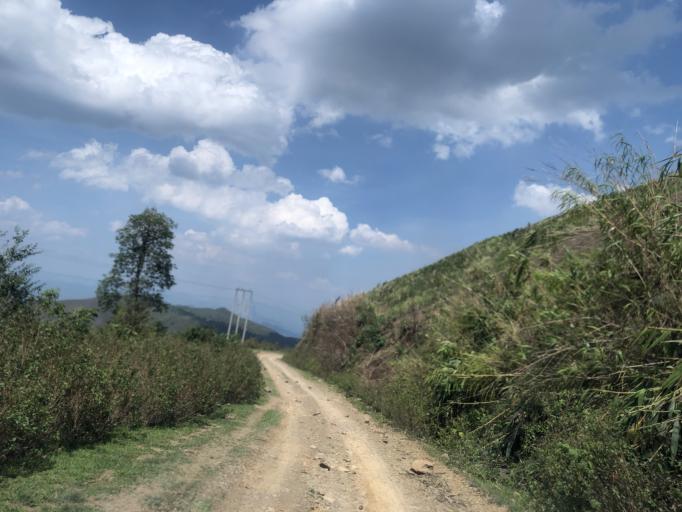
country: LA
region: Phongsali
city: Phongsali
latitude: 21.3971
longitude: 102.2149
